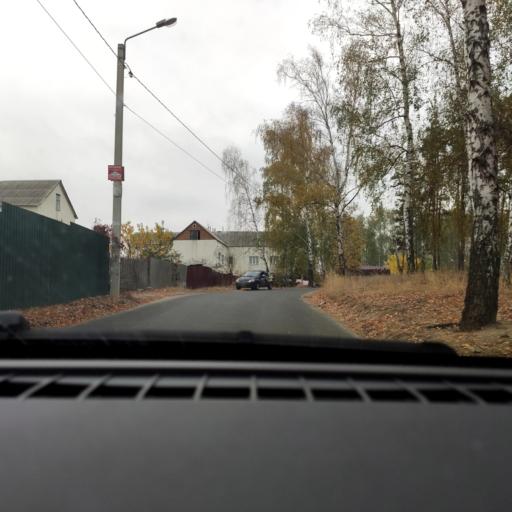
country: RU
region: Voronezj
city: Somovo
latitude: 51.7437
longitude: 39.3217
